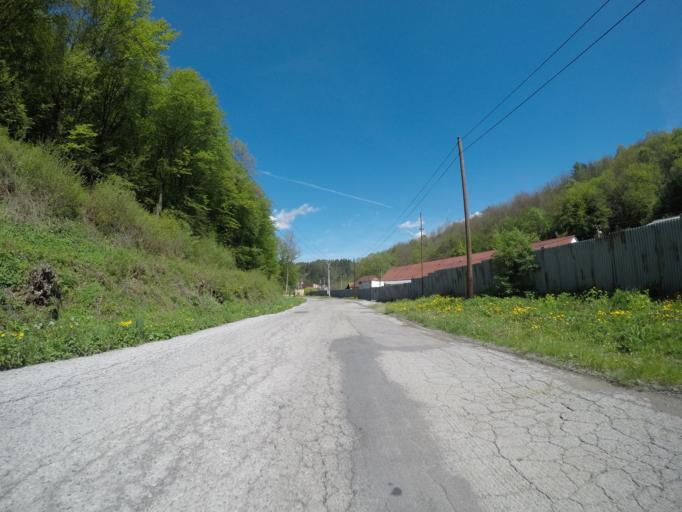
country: SK
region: Banskobystricky
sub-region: Okres Banska Bystrica
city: Banska Bystrica
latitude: 48.7158
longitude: 19.2277
